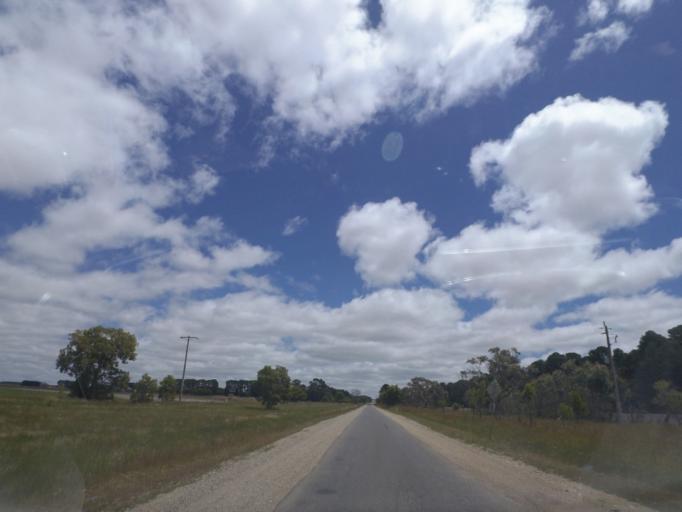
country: AU
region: Victoria
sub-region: Moorabool
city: Bacchus Marsh
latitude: -37.6414
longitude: 144.2853
